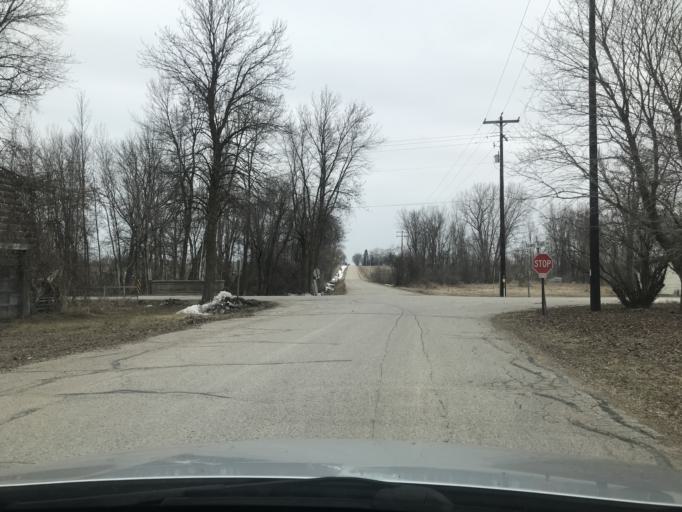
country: US
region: Wisconsin
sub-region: Marinette County
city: Peshtigo
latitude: 45.0483
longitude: -87.8511
